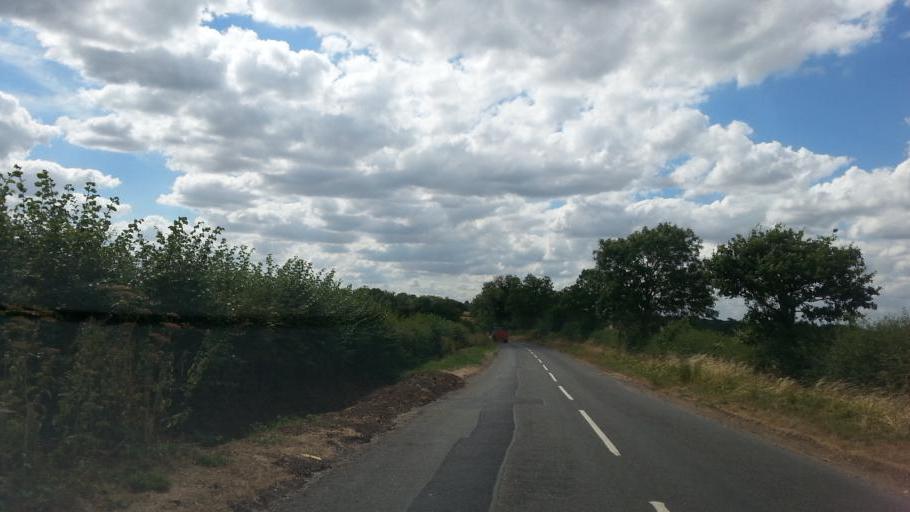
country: GB
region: England
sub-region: Northamptonshire
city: Silverstone
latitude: 52.0934
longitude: -1.0003
